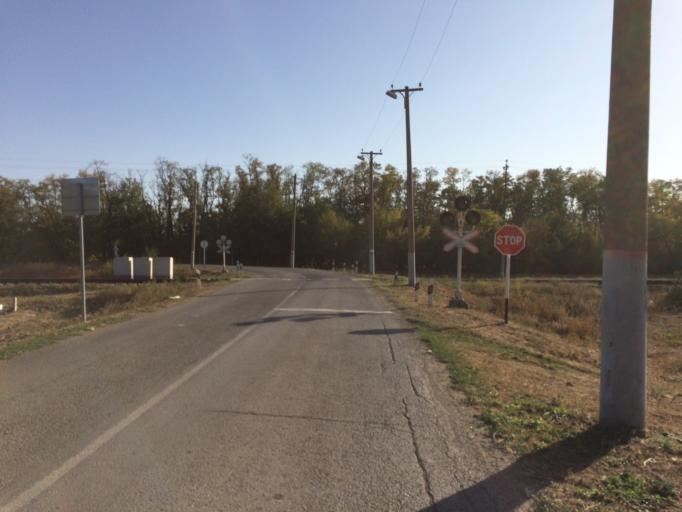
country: RU
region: Rostov
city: Tselina
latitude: 46.5287
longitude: 41.1880
